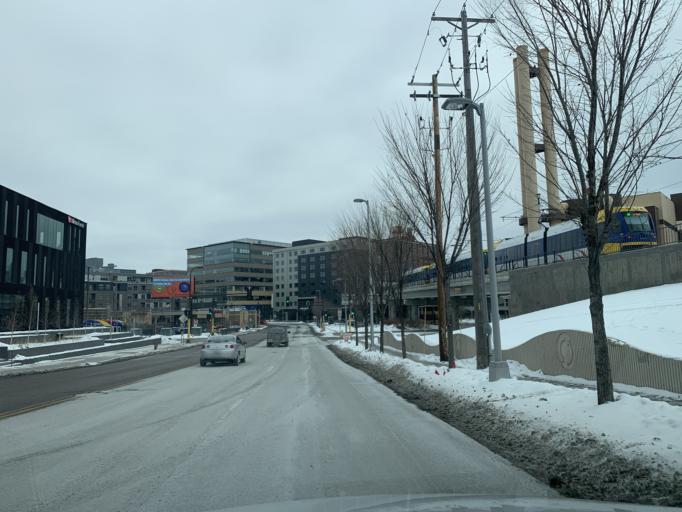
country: US
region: Minnesota
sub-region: Hennepin County
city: Minneapolis
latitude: 44.9844
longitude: -93.2817
